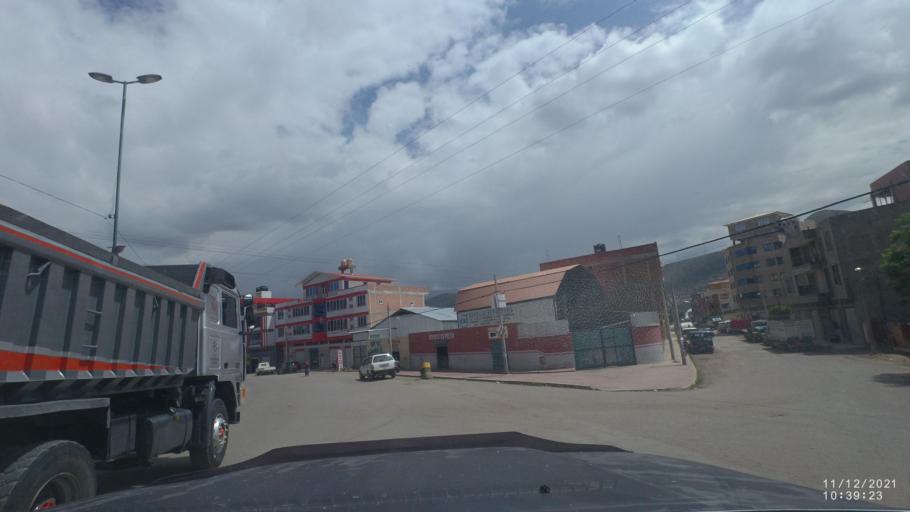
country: BO
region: Cochabamba
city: Cochabamba
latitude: -17.4360
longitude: -66.1251
